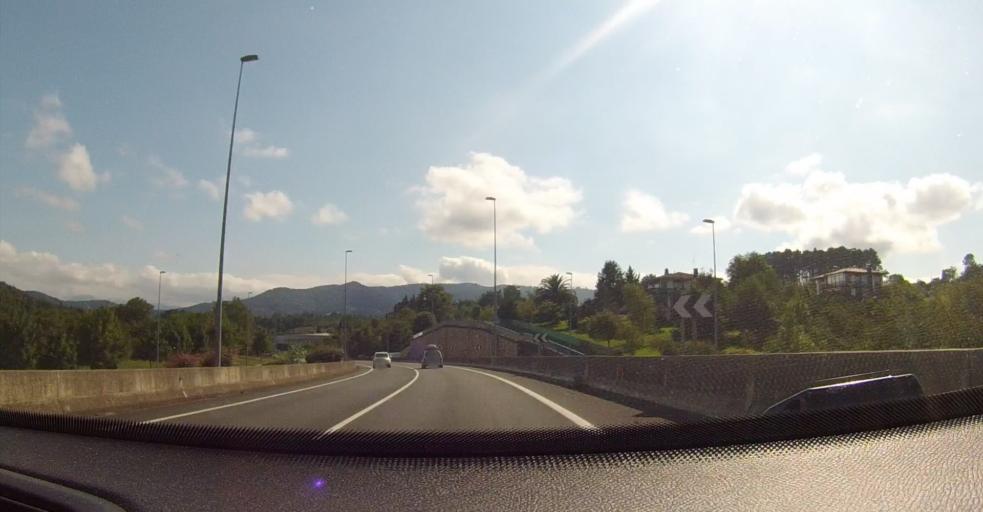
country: ES
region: Basque Country
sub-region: Bizkaia
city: Muxika
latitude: 43.3008
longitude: -2.6852
